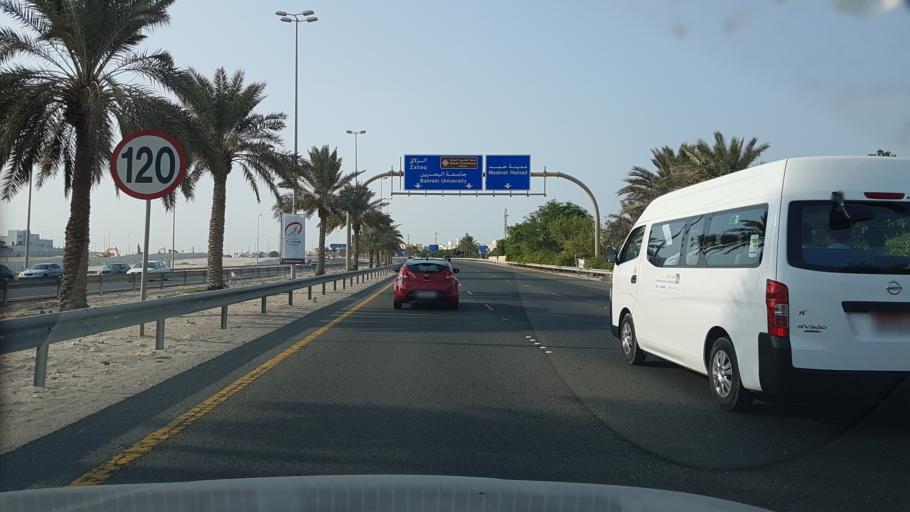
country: BH
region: Central Governorate
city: Madinat Hamad
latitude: 26.1308
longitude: 50.5079
